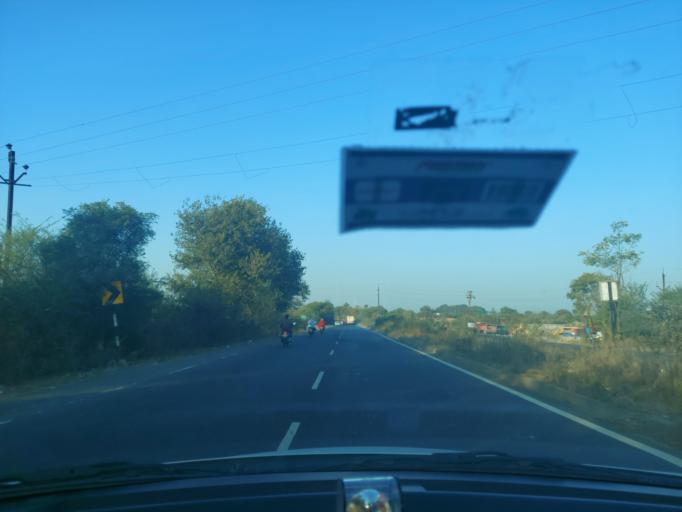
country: IN
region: Madhya Pradesh
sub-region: Indore
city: Sanwer
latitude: 23.0394
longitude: 75.8283
